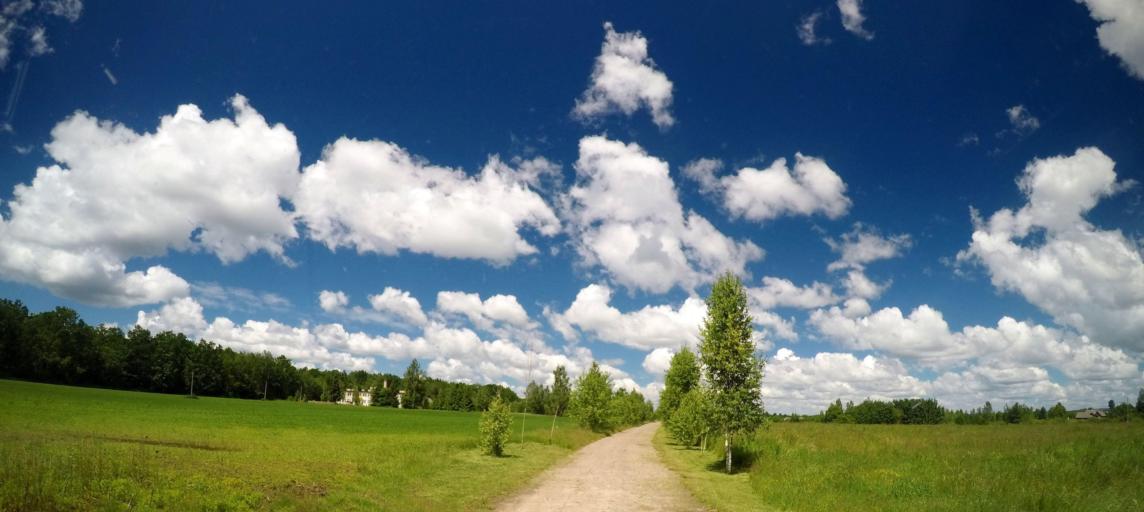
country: BY
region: Grodnenskaya
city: Hal'shany
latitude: 54.1654
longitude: 26.0838
